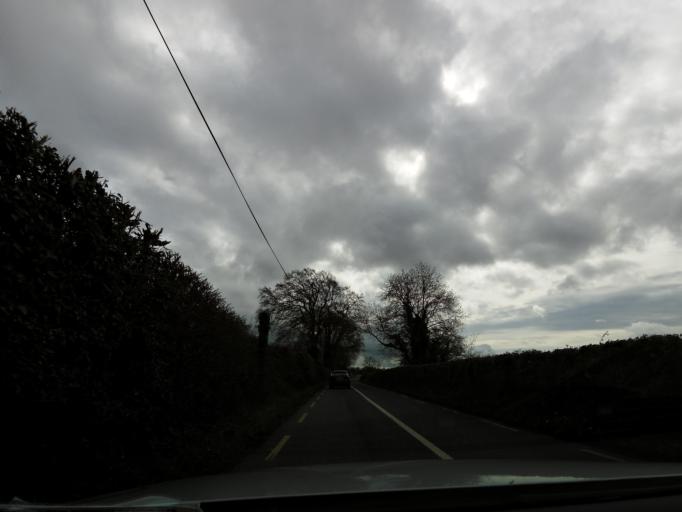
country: IE
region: Leinster
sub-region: Laois
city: Rathdowney
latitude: 52.7237
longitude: -7.5252
